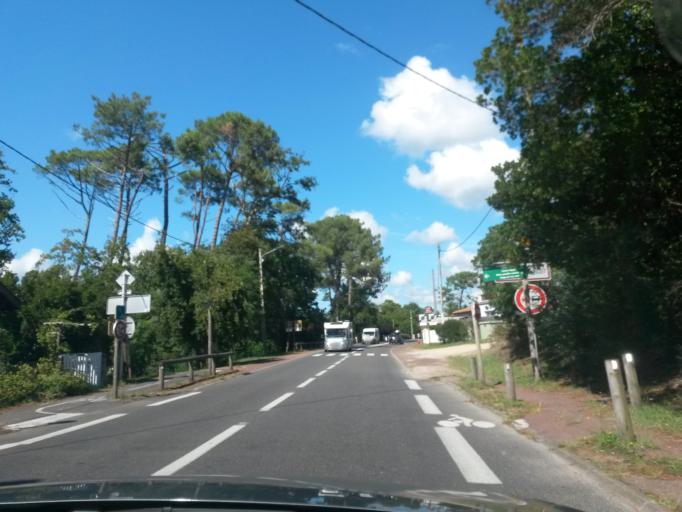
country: FR
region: Aquitaine
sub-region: Departement de la Gironde
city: Arcachon
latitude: 44.7205
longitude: -1.2101
